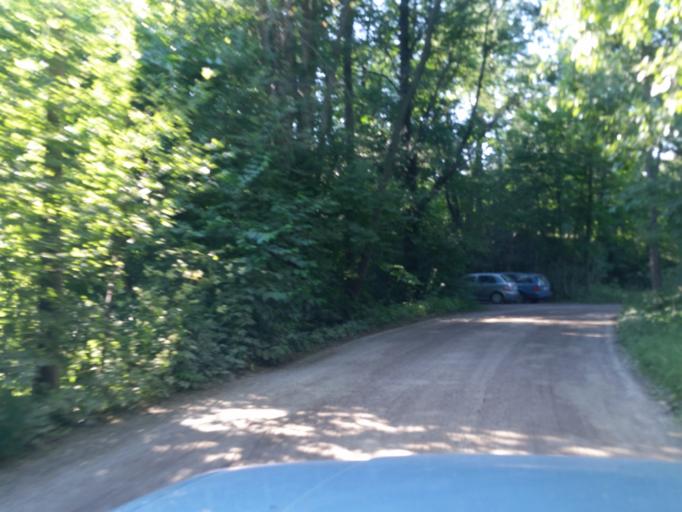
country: FI
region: Uusimaa
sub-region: Helsinki
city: Helsinki
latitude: 60.1937
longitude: 25.0148
